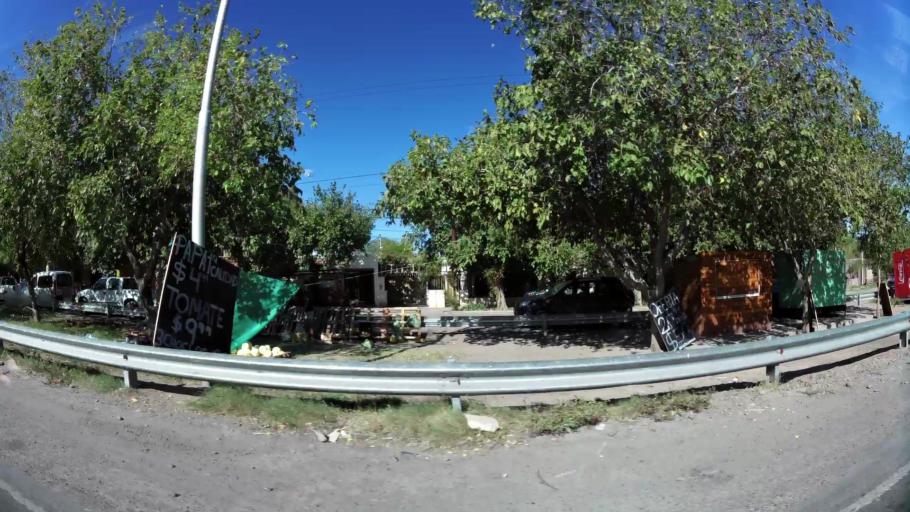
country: AR
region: San Juan
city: Villa Paula de Sarmiento
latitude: -31.5121
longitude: -68.5176
